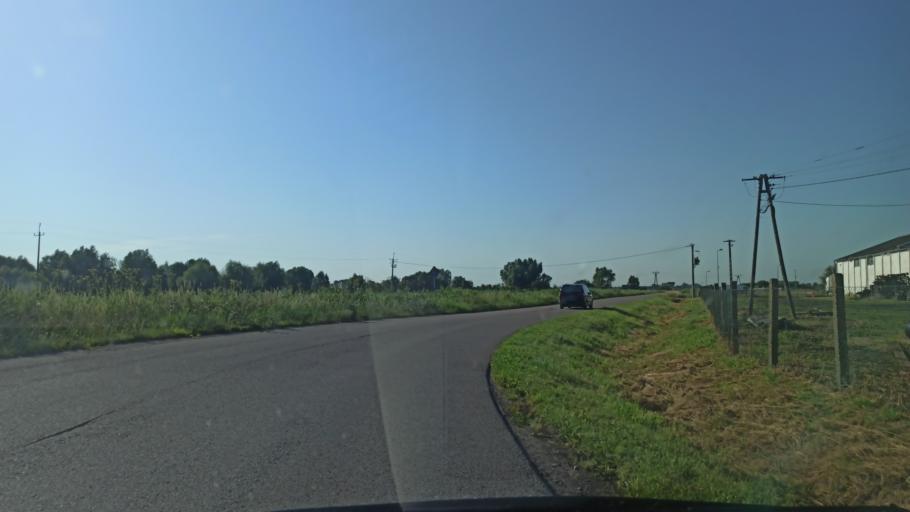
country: PL
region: Warmian-Masurian Voivodeship
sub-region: Powiat elblaski
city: Elblag
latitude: 54.1894
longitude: 19.3315
